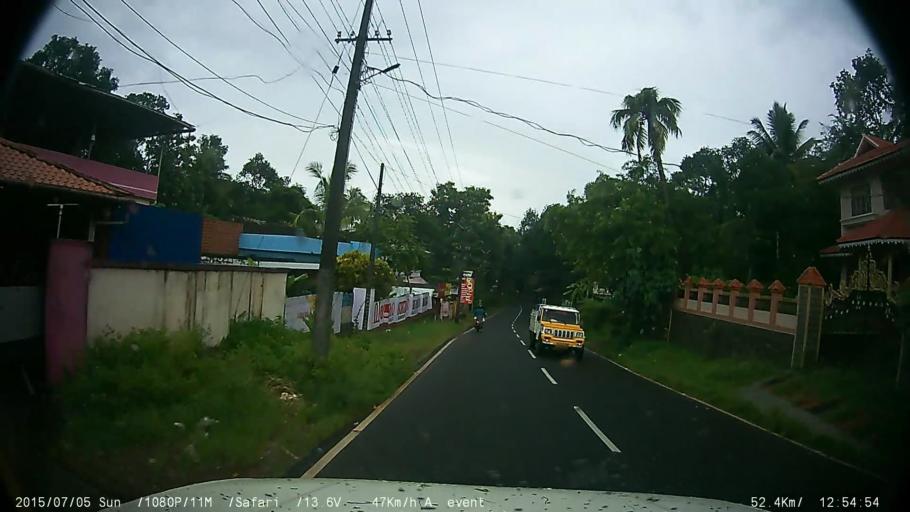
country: IN
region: Kerala
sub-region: Kottayam
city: Changanacheri
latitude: 9.4500
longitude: 76.5745
